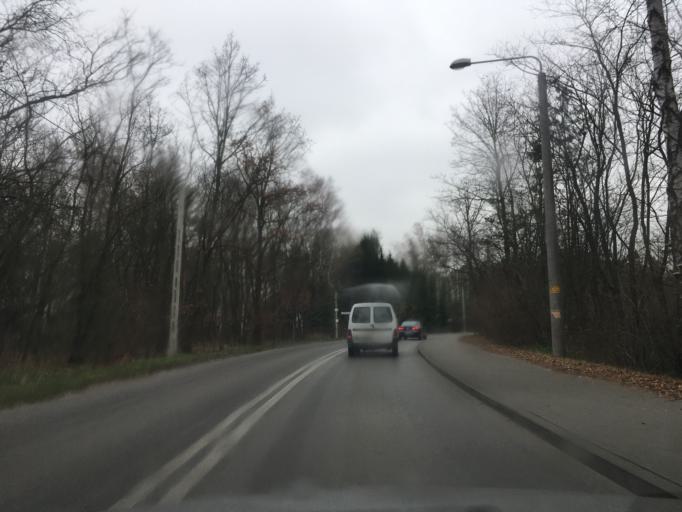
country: PL
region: Masovian Voivodeship
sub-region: Powiat piaseczynski
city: Lesznowola
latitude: 52.0621
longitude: 20.9193
